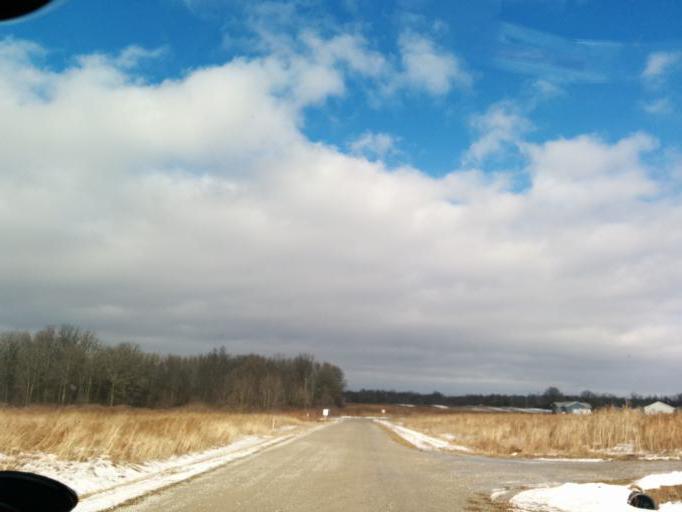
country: CA
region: Ontario
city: Brantford
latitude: 43.0109
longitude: -80.0916
